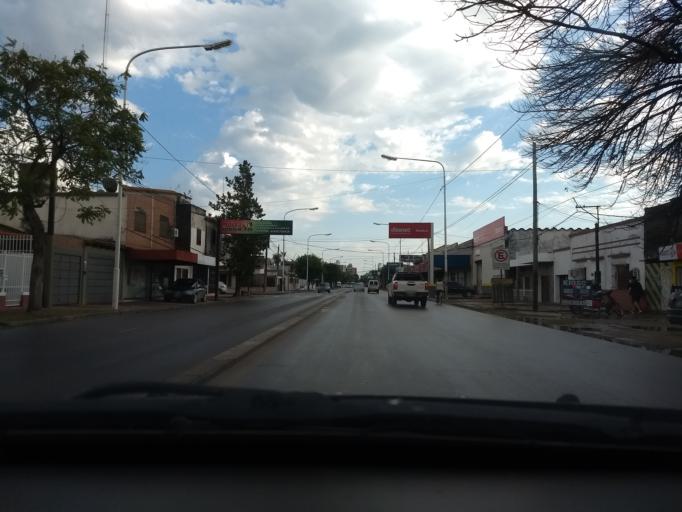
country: AR
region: Corrientes
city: Corrientes
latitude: -27.4818
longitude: -58.8268
